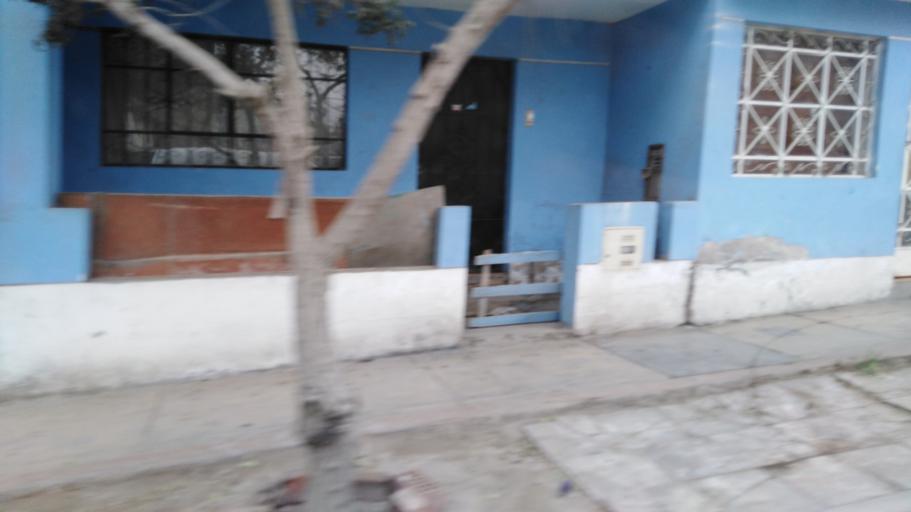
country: PE
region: Lima
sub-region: Lima
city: Surco
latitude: -12.1438
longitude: -76.9474
